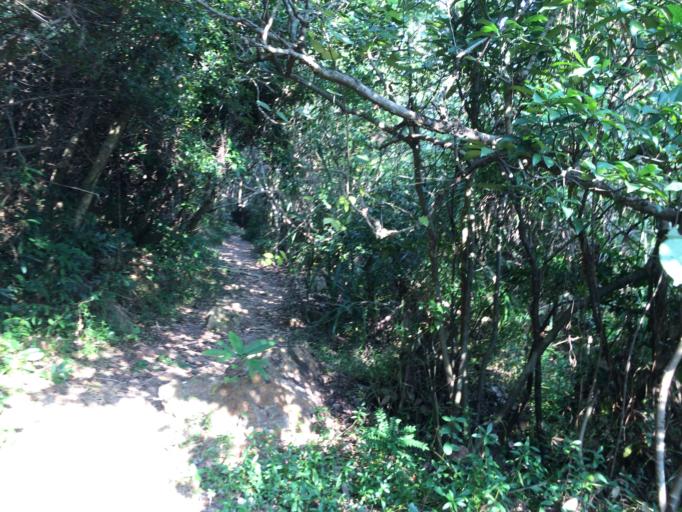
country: HK
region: Tai Po
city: Tai Po
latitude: 22.4507
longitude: 114.2277
